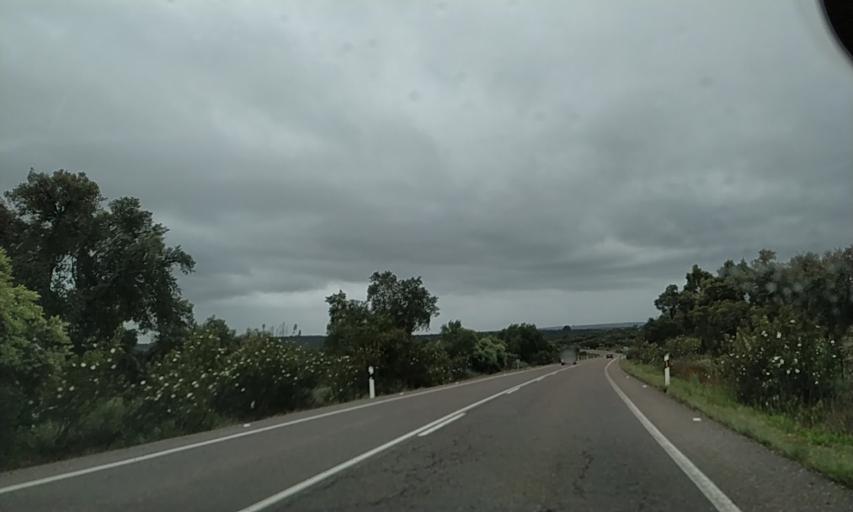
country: ES
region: Extremadura
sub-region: Provincia de Badajoz
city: Puebla de Obando
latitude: 39.1518
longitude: -6.6483
